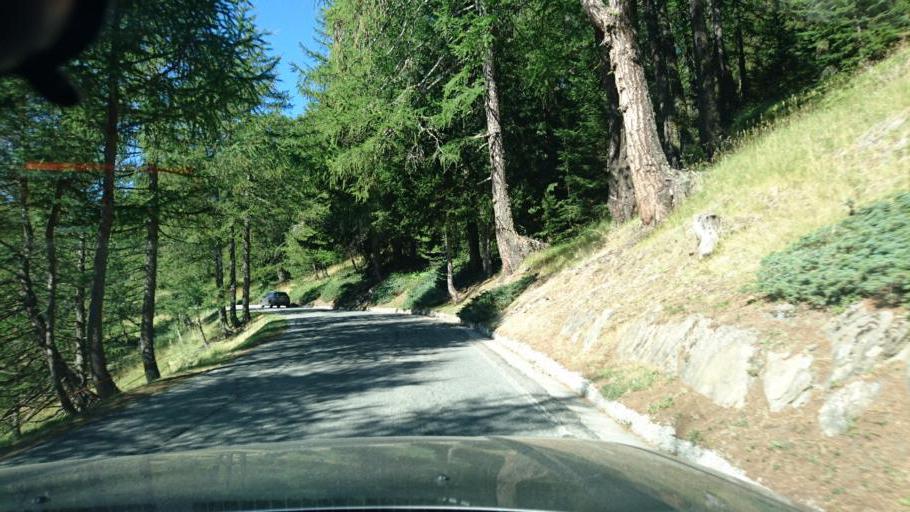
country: IT
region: Aosta Valley
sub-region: Valle d'Aosta
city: Pre Saint Didier
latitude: 45.7435
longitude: 6.9954
